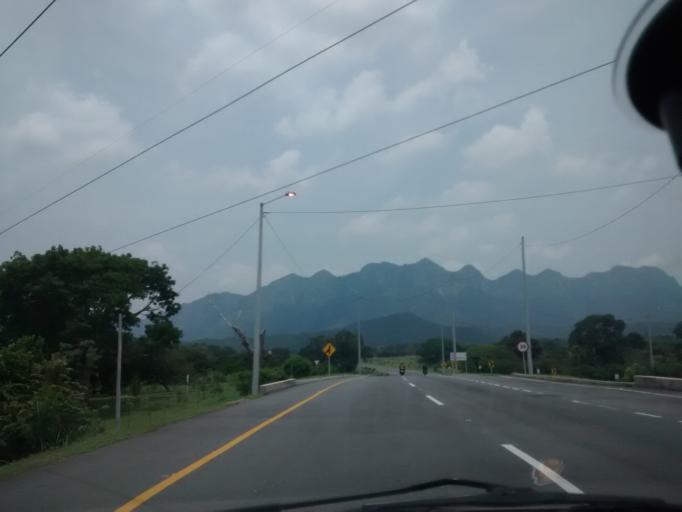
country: CO
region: Tolima
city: Valle de San Juan
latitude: 4.2682
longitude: -74.9989
